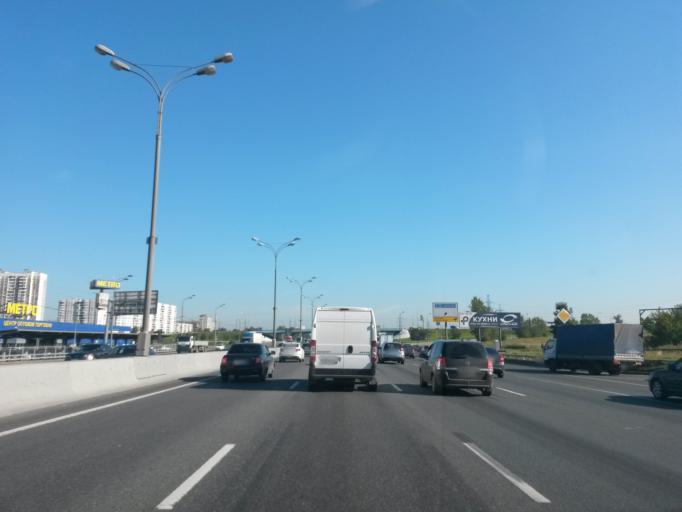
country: RU
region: Moscow
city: Vostochnyy
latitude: 55.8102
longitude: 37.8394
